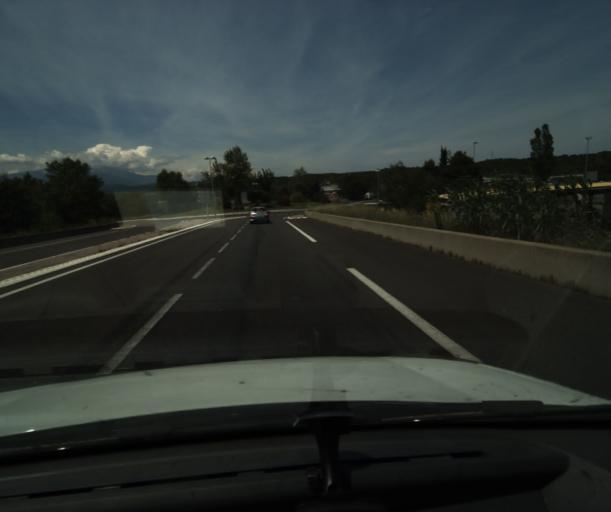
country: FR
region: Languedoc-Roussillon
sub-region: Departement des Pyrenees-Orientales
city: el Volo
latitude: 42.5212
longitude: 2.8181
